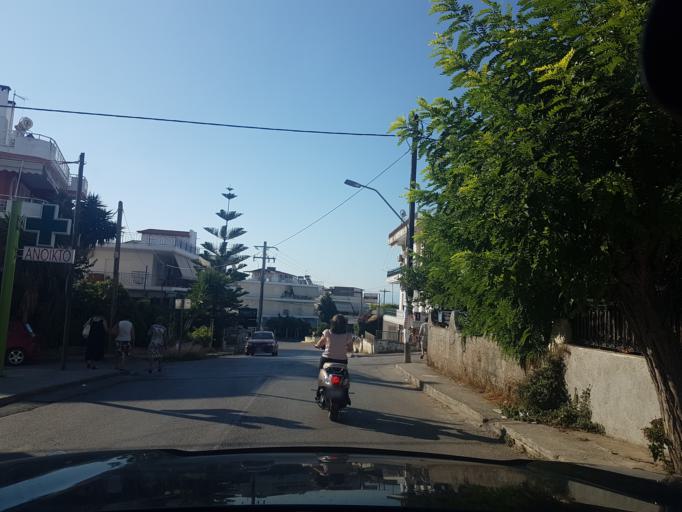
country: GR
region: Central Greece
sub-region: Nomos Evvoias
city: Chalkida
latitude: 38.4713
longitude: 23.5859
